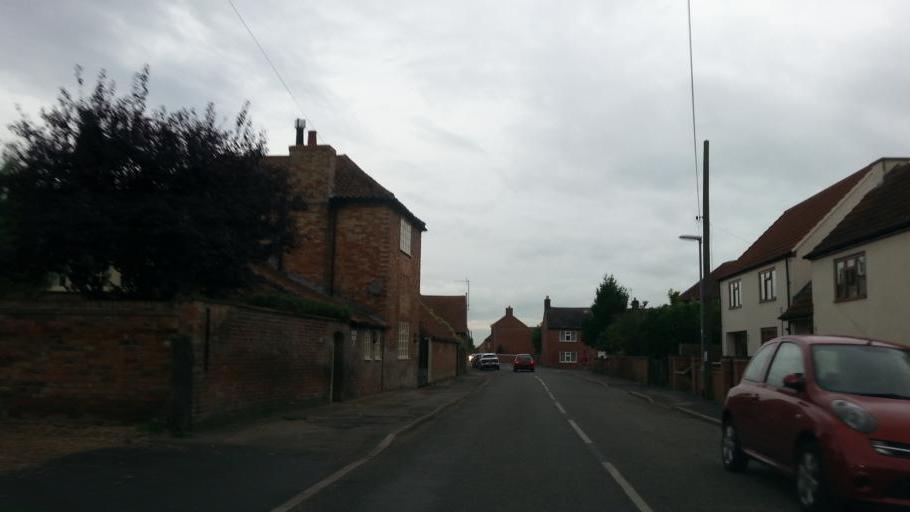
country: GB
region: England
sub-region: Lincolnshire
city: Long Bennington
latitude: 53.0318
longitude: -0.7354
